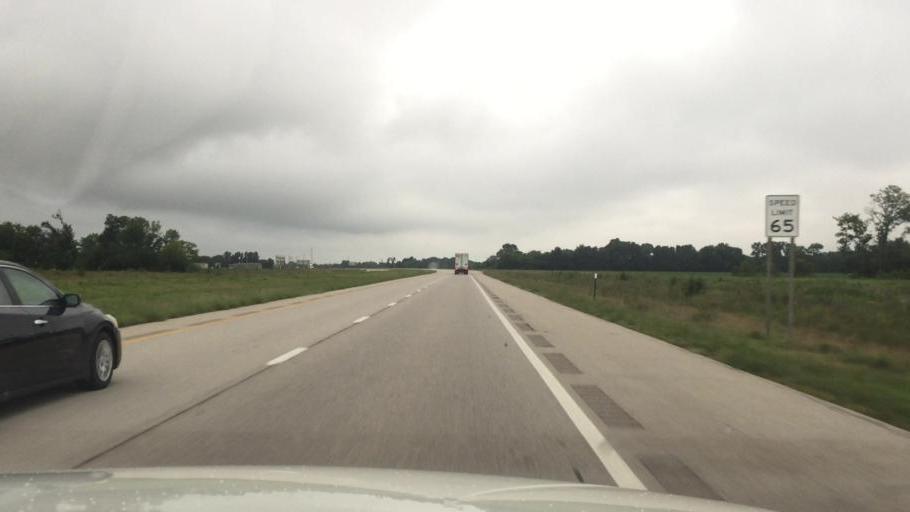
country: US
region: Kansas
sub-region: Montgomery County
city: Coffeyville
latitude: 37.1056
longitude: -95.5879
